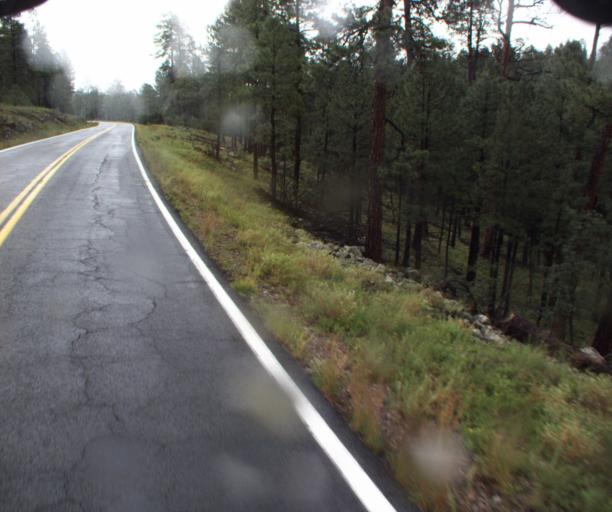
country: US
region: Arizona
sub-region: Apache County
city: Eagar
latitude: 33.7691
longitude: -109.1956
